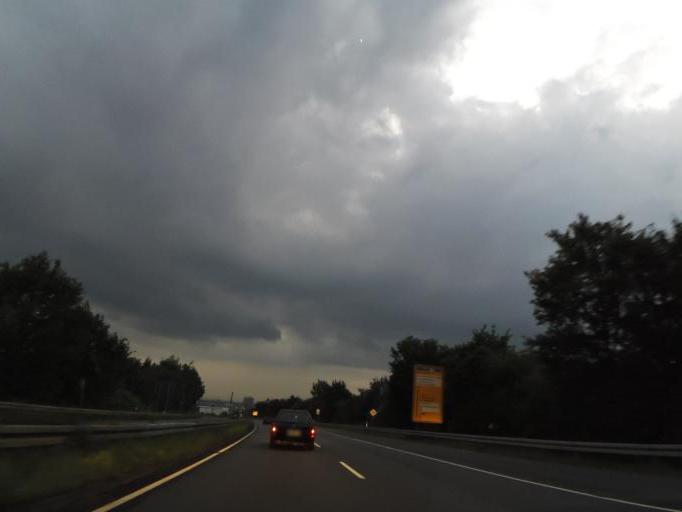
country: DE
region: Hesse
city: Langen
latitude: 49.9954
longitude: 8.6843
